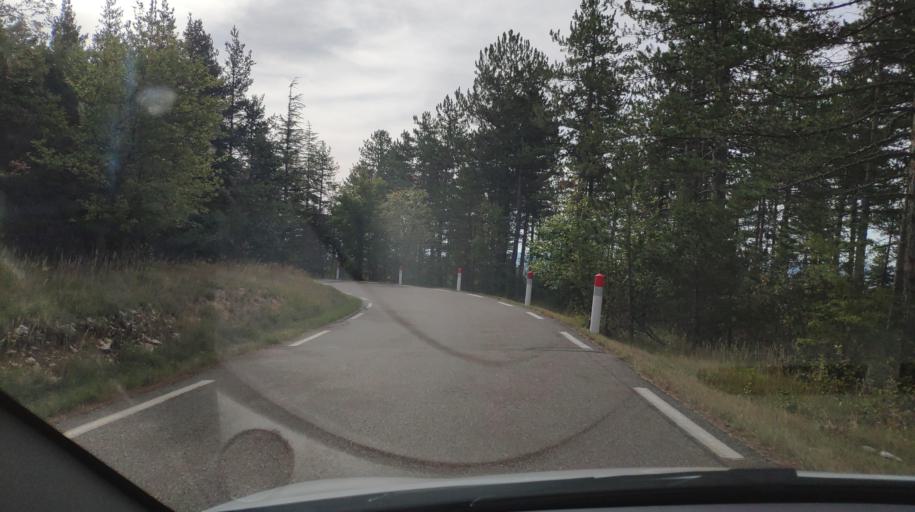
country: FR
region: Provence-Alpes-Cote d'Azur
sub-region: Departement du Vaucluse
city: Sault
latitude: 44.1454
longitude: 5.3636
